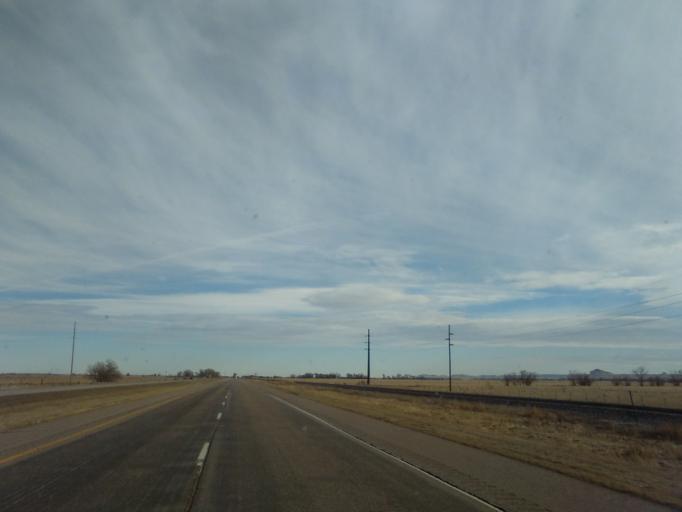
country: US
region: Nebraska
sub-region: Scotts Bluff County
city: Gering
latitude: 41.8260
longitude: -103.5609
